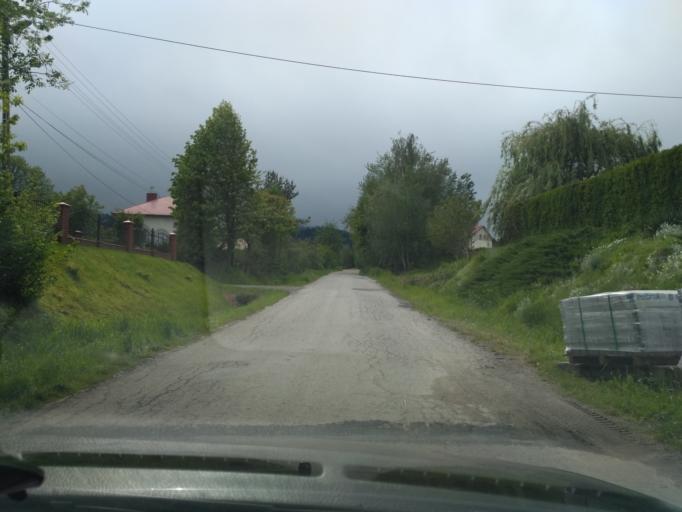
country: PL
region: Subcarpathian Voivodeship
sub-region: Powiat jasielski
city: Brzyska
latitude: 49.8243
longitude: 21.3718
